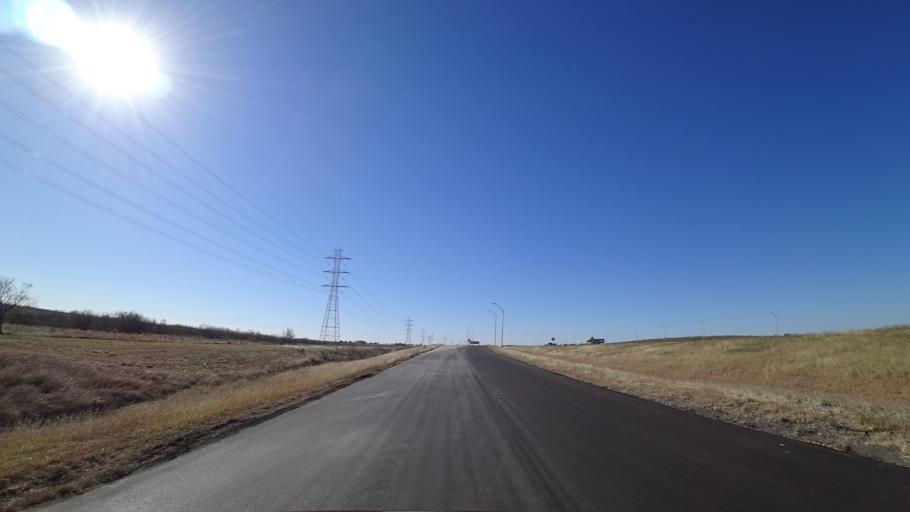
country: US
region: Texas
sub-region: Travis County
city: Onion Creek
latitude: 30.1141
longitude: -97.6610
